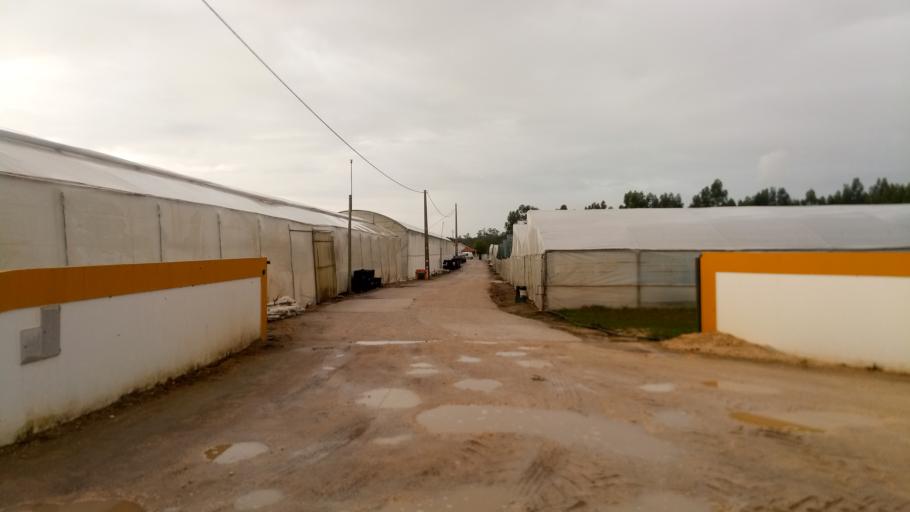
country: PT
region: Leiria
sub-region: Caldas da Rainha
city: Caldas da Rainha
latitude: 39.4359
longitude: -9.1635
